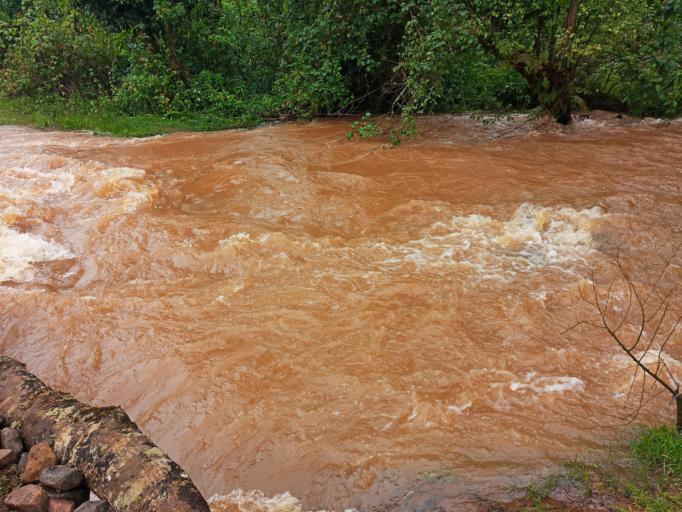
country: ET
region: Oromiya
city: Hagere Maryam
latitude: 5.9713
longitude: 38.4081
